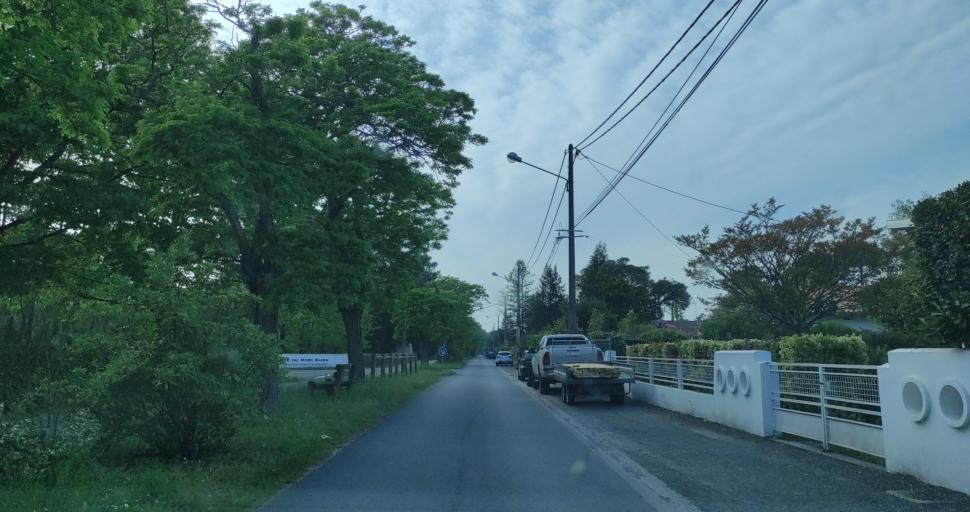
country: FR
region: Aquitaine
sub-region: Departement de la Gironde
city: Ares
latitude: 44.7541
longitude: -1.1286
